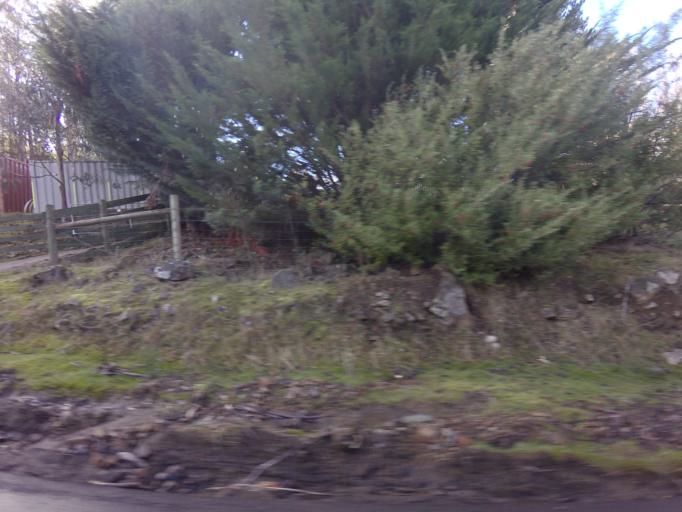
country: AU
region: Tasmania
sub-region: Glenorchy
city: Berriedale
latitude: -42.8502
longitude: 147.1684
